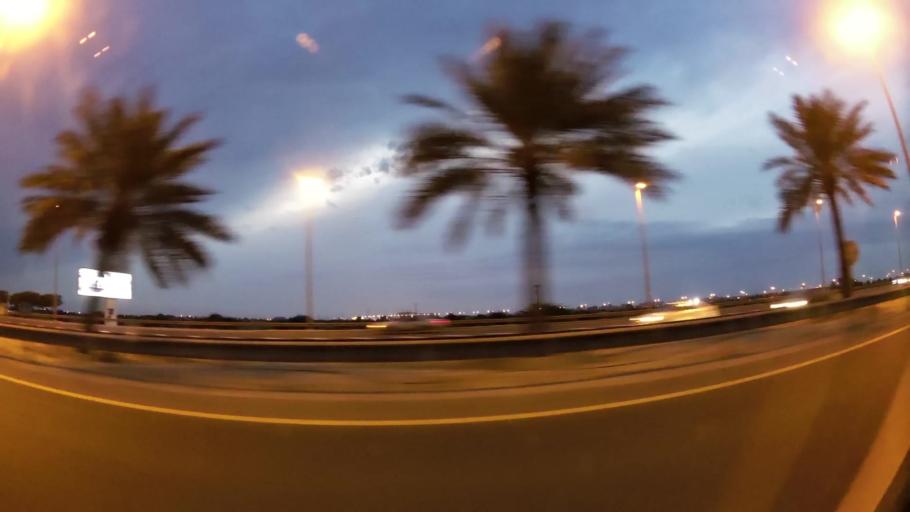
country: BH
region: Northern
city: Madinat `Isa
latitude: 26.1767
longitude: 50.5024
